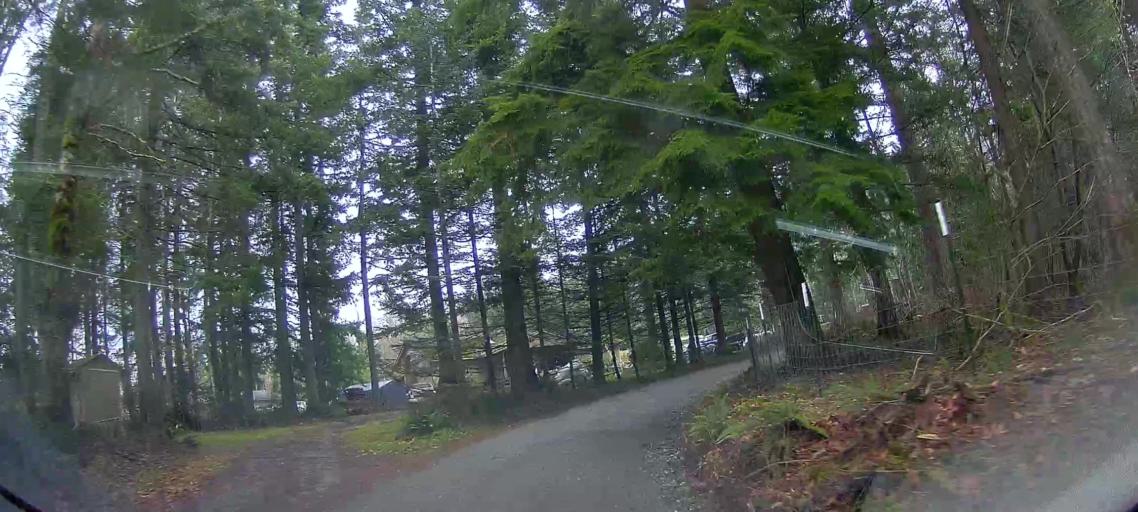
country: US
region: Washington
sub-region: Skagit County
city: Sedro-Woolley
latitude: 48.5958
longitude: -122.2210
